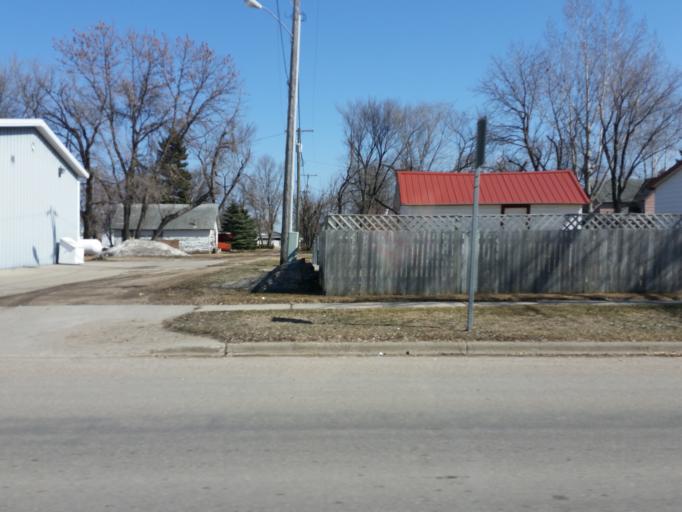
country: US
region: North Dakota
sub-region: Walsh County
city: Grafton
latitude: 48.2900
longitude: -97.3714
